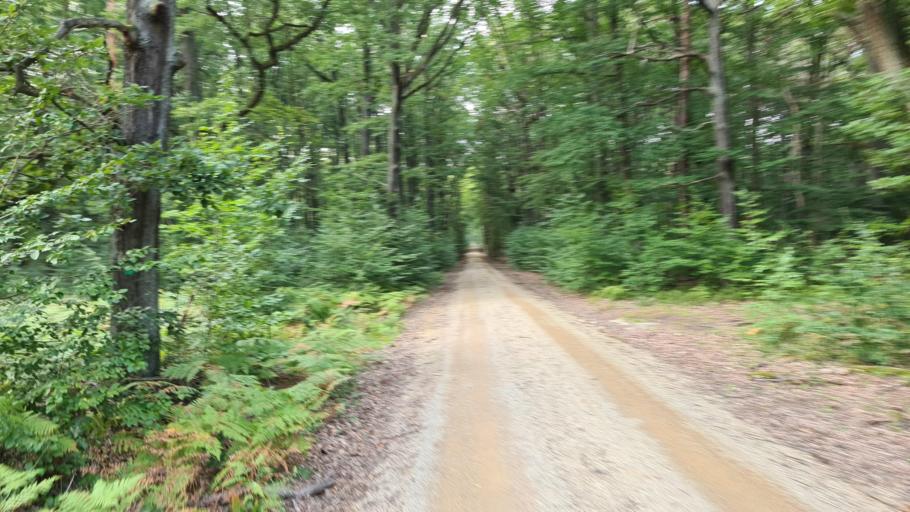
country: DE
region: Brandenburg
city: Trobitz
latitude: 51.6288
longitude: 13.4545
